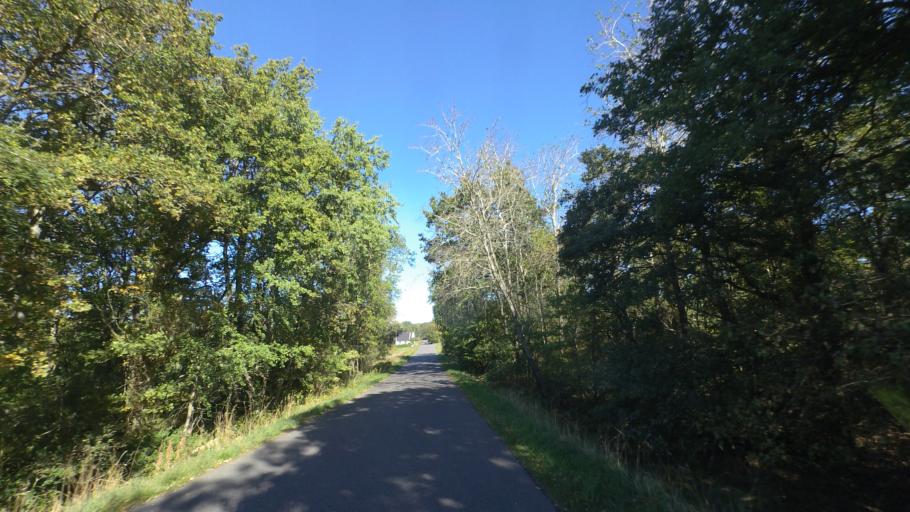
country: DK
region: Capital Region
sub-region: Bornholm Kommune
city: Nexo
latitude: 55.0763
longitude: 15.0802
